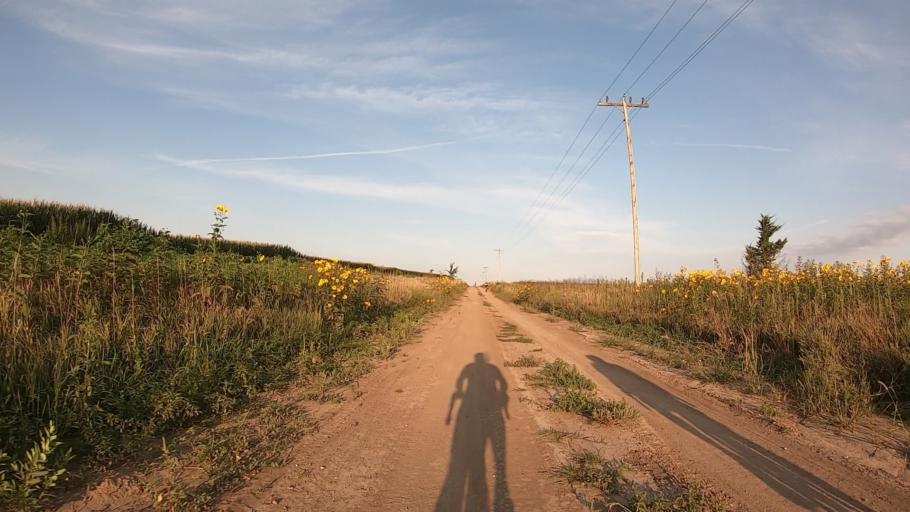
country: US
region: Kansas
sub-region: Marshall County
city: Marysville
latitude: 39.7692
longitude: -96.7292
